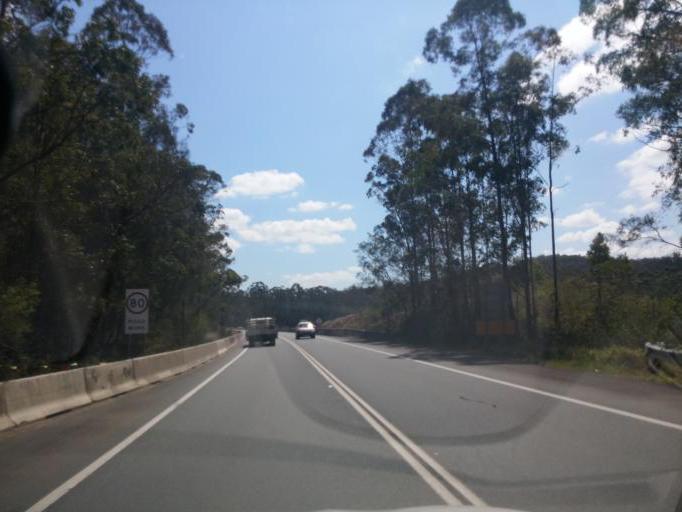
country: AU
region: New South Wales
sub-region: Port Macquarie-Hastings
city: North Shore
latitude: -31.3048
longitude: 152.8214
